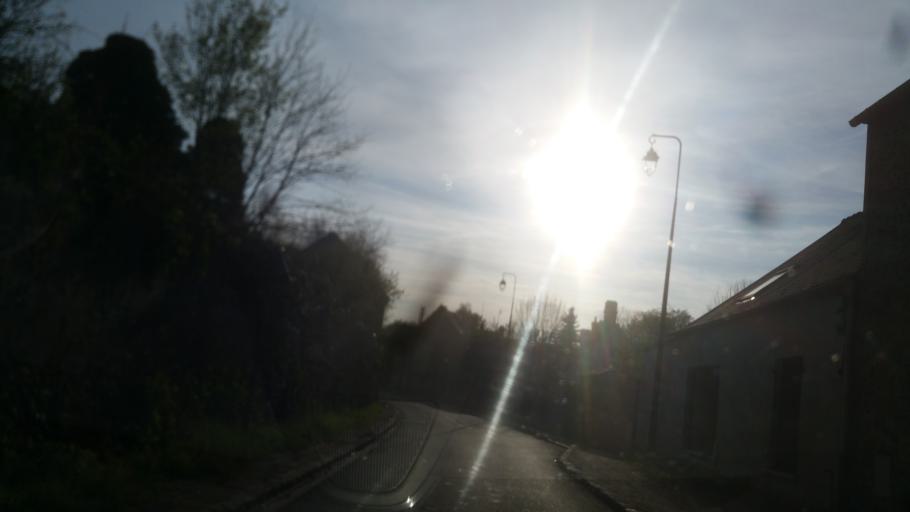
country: FR
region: Ile-de-France
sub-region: Departement de l'Essonne
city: Saint-Maurice-Montcouronne
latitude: 48.5758
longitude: 2.1001
